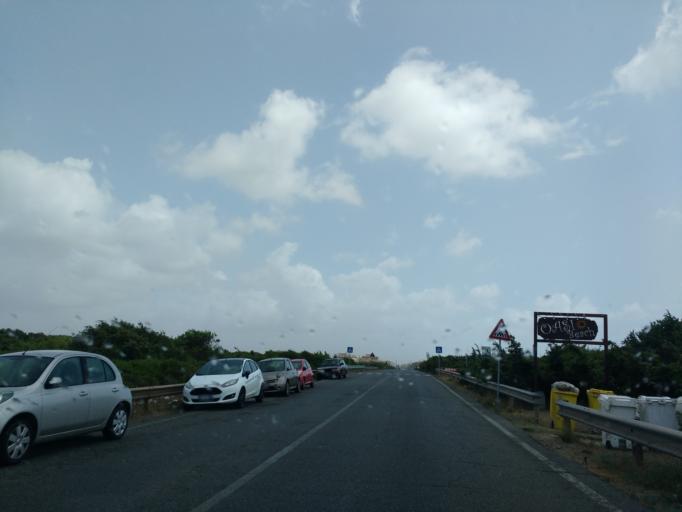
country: IT
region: Latium
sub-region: Citta metropolitana di Roma Capitale
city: Torvaianica
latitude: 41.6516
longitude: 12.4239
